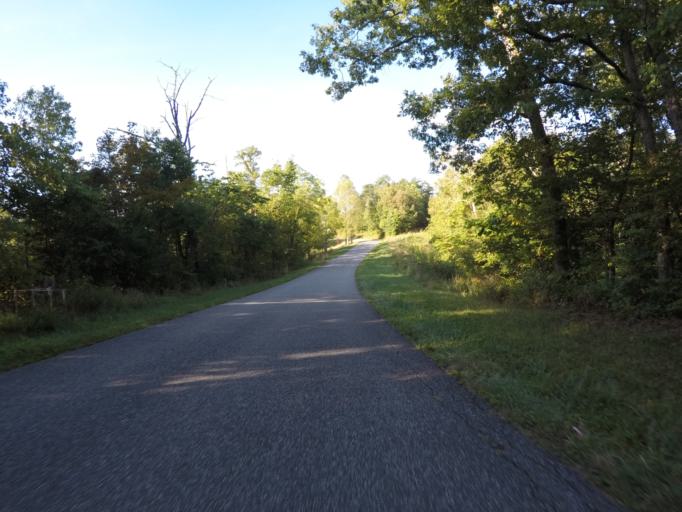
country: US
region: Ohio
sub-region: Lawrence County
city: Coal Grove
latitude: 38.6013
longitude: -82.5549
